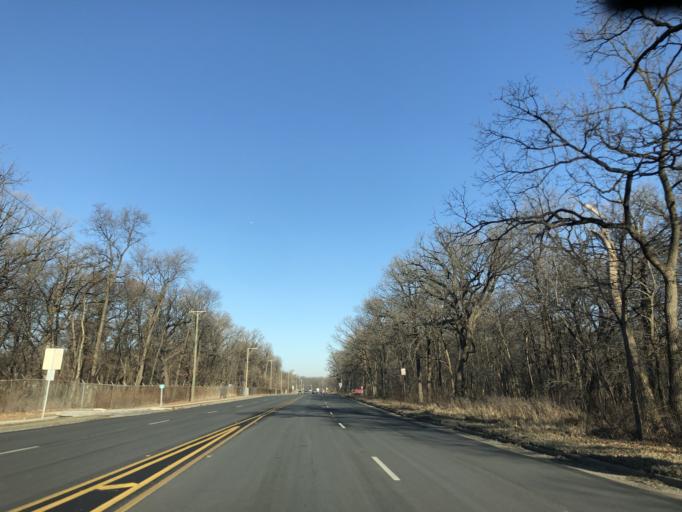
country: US
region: Illinois
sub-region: Cook County
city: Riverside
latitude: 41.8295
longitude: -87.8289
